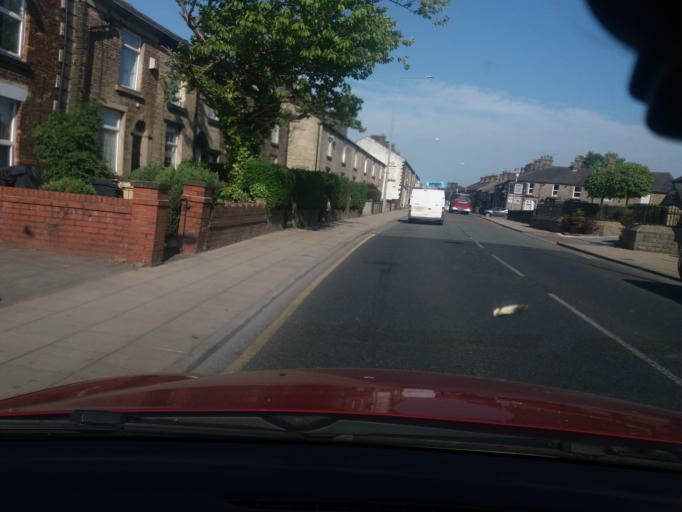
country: GB
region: England
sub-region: Borough of Bolton
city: Horwich
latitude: 53.6014
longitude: -2.5499
